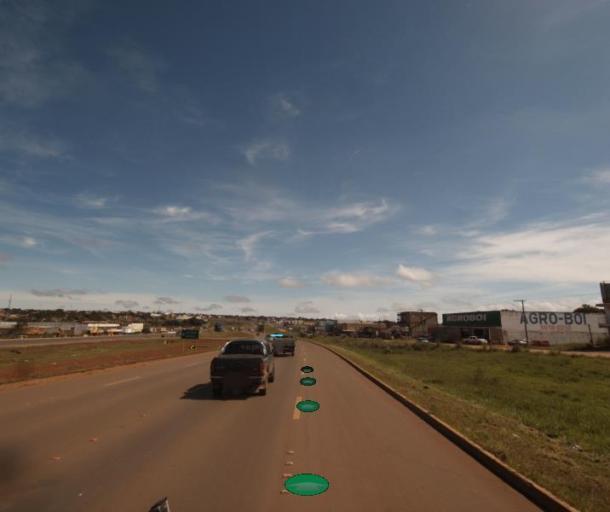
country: BR
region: Federal District
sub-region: Brasilia
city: Brasilia
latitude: -15.7429
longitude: -48.2686
